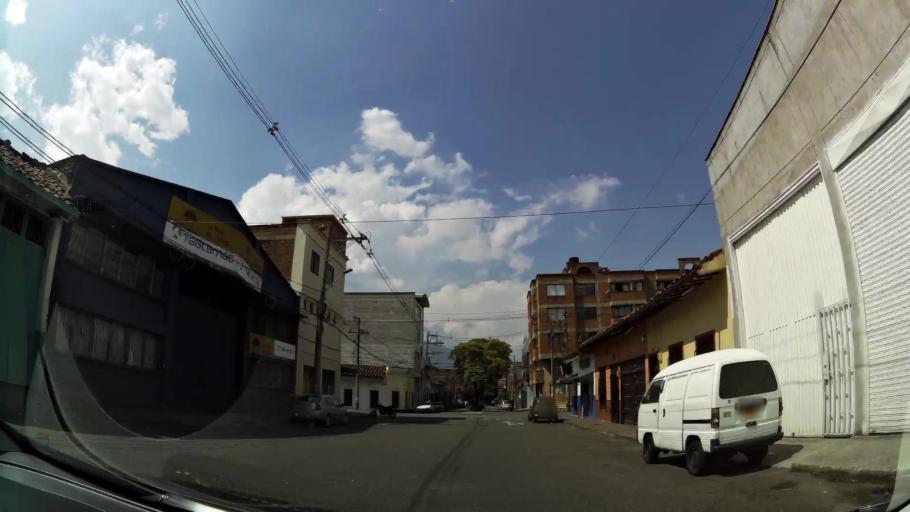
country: CO
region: Antioquia
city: Medellin
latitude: 6.2303
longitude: -75.5927
